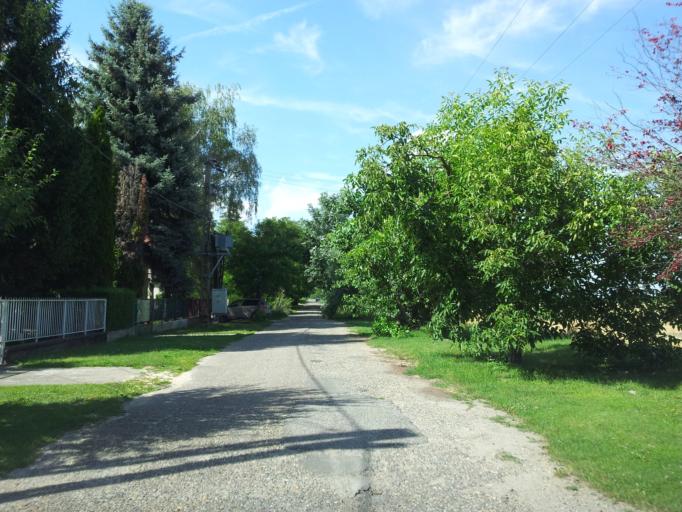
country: HU
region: Pest
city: Szigetcsep
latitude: 47.2383
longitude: 18.9780
